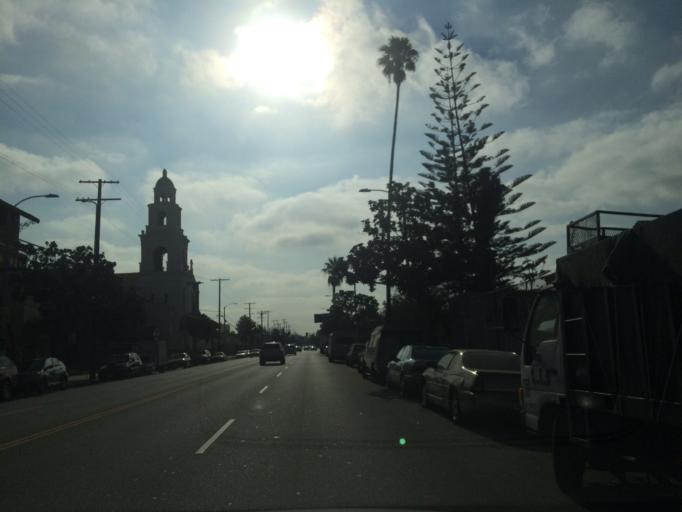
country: US
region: California
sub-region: Los Angeles County
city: Los Angeles
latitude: 34.0328
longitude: -118.2942
